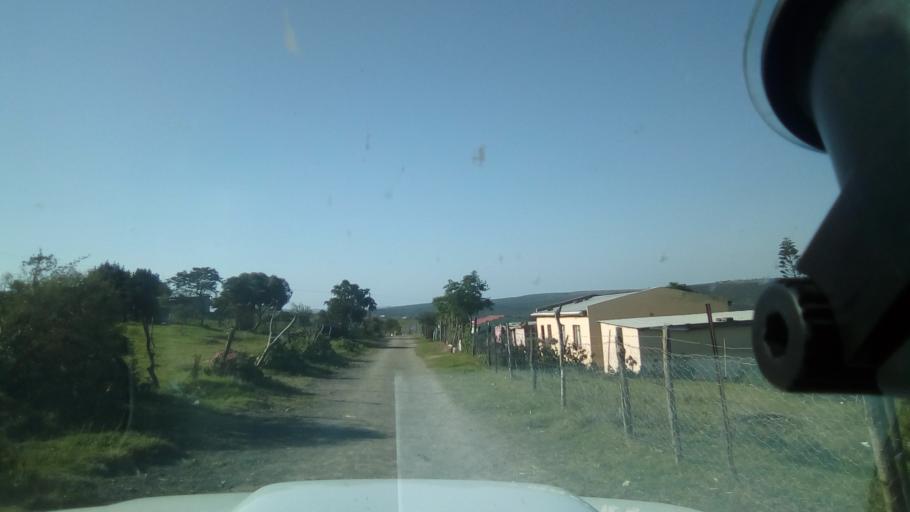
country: ZA
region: Eastern Cape
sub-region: Buffalo City Metropolitan Municipality
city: Bhisho
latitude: -32.8108
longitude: 27.3538
